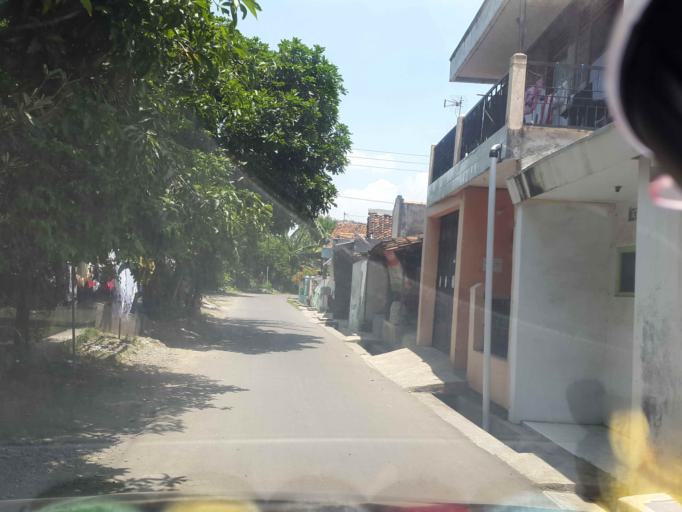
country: ID
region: Central Java
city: Tegal
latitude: -6.8745
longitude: 109.1384
